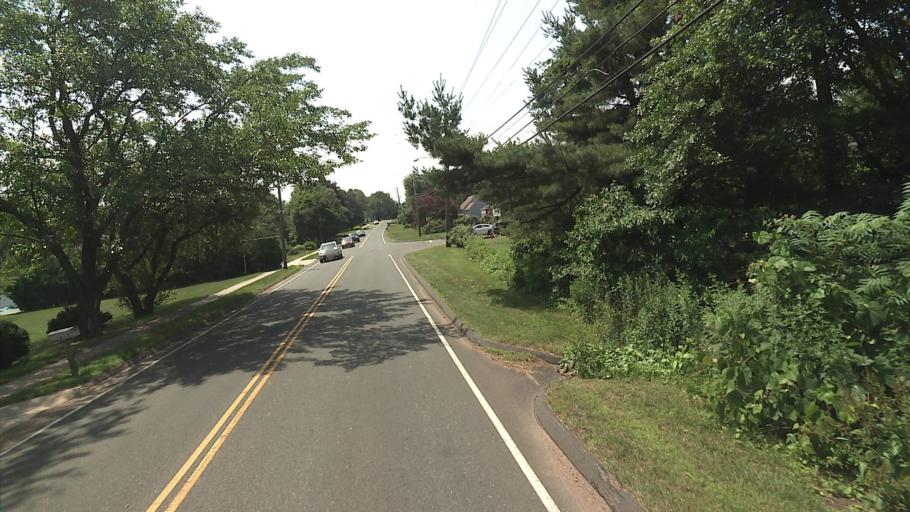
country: US
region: Connecticut
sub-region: New Haven County
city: Branford
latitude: 41.3071
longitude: -72.8197
